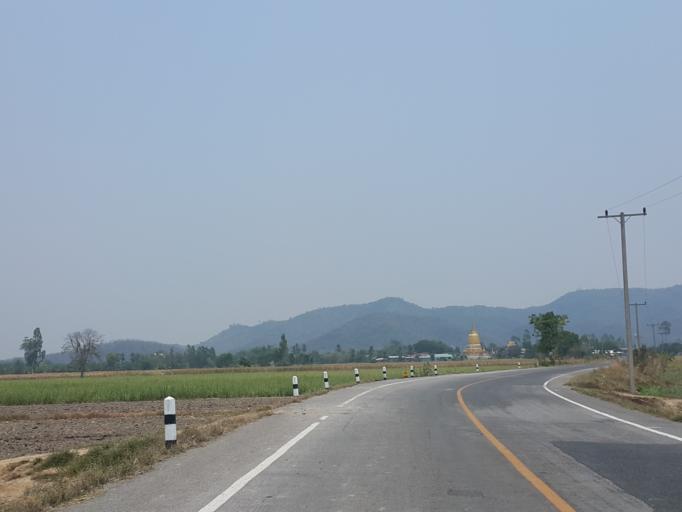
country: TH
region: Kamphaeng Phet
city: Pang Sila Thong
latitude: 16.0559
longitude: 99.3697
